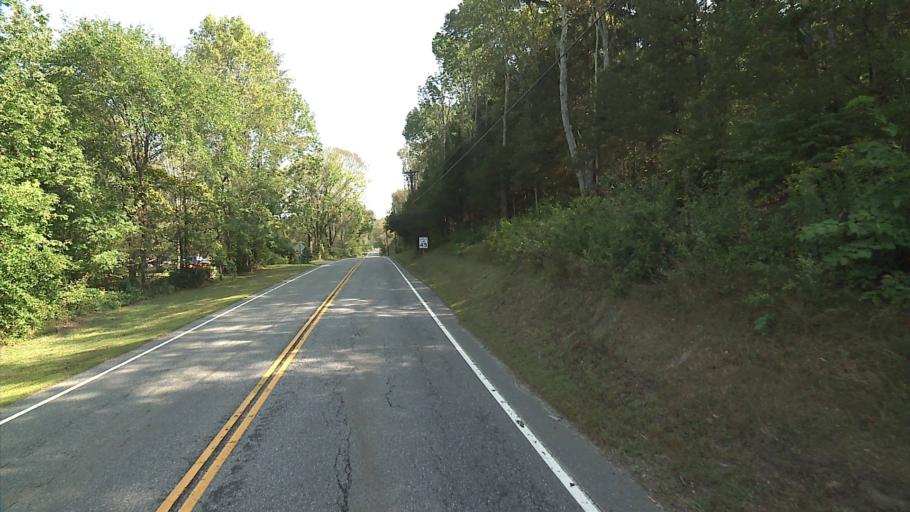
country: US
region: Connecticut
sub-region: New London County
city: Jewett City
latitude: 41.6393
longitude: -71.9931
